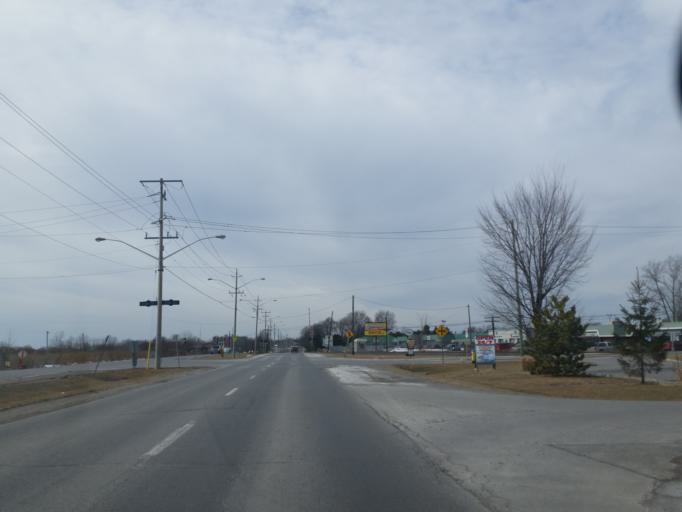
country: CA
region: Ontario
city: Belleville
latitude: 44.1692
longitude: -77.3387
